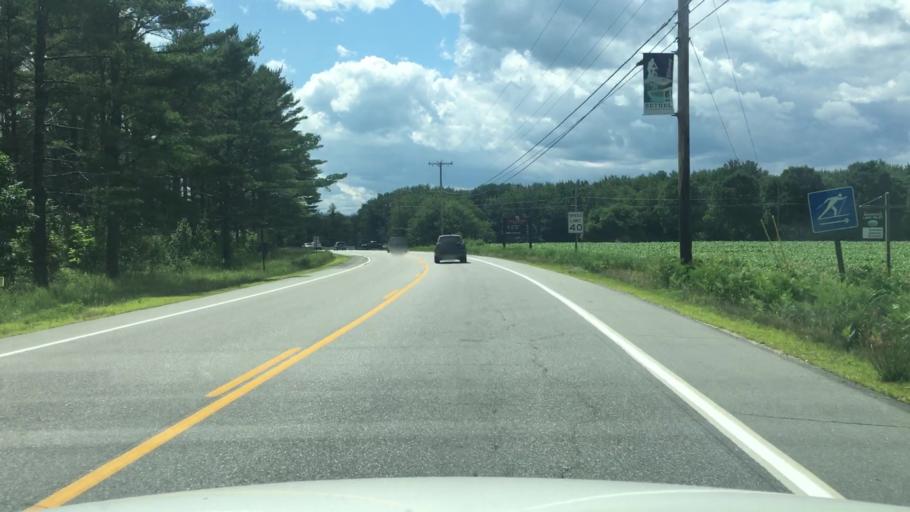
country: US
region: Maine
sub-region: Oxford County
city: Bethel
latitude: 44.4160
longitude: -70.7821
